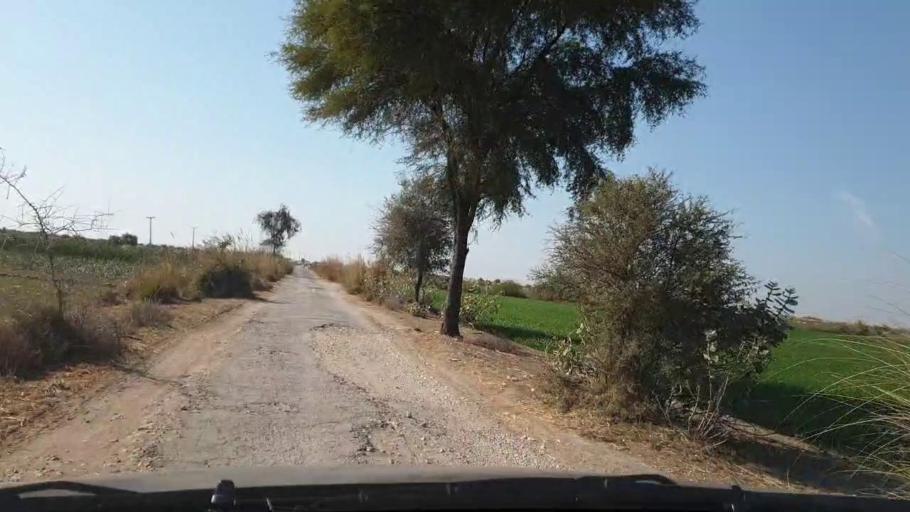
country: PK
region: Sindh
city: Khadro
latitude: 26.2678
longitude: 68.8027
